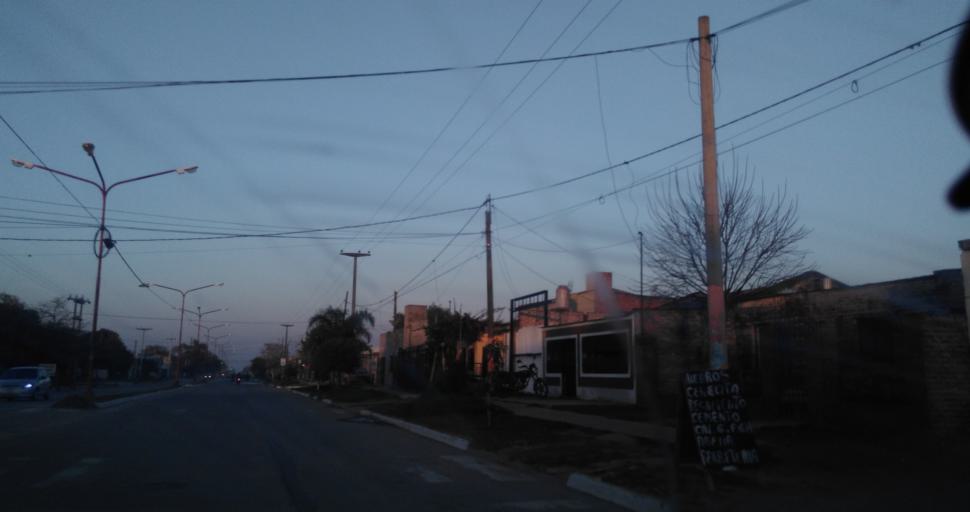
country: AR
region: Chaco
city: Resistencia
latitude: -27.4873
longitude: -58.9840
